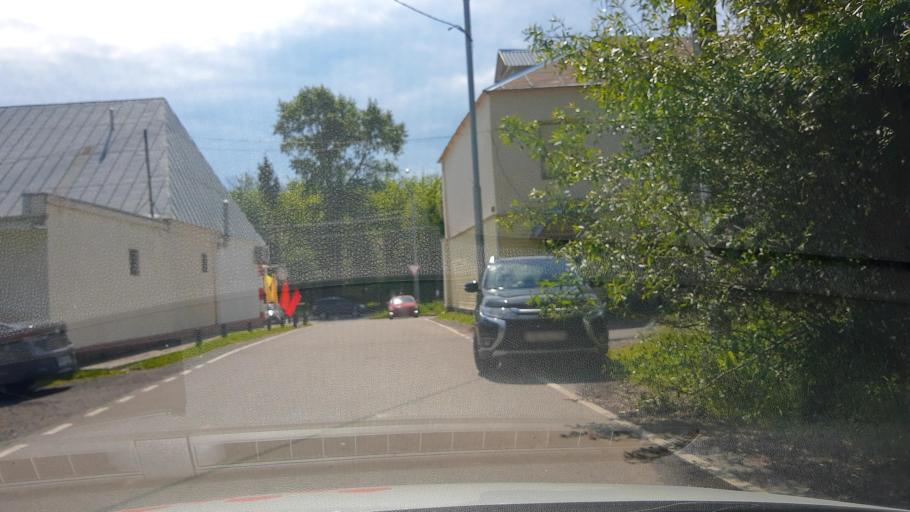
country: RU
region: Moskovskaya
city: Kievskij
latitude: 55.2203
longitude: 36.9926
